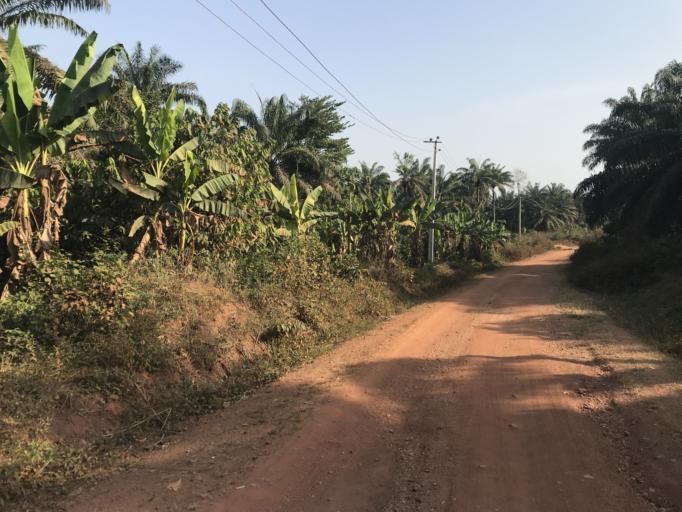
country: NG
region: Osun
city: Awo
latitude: 7.7590
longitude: 4.3163
